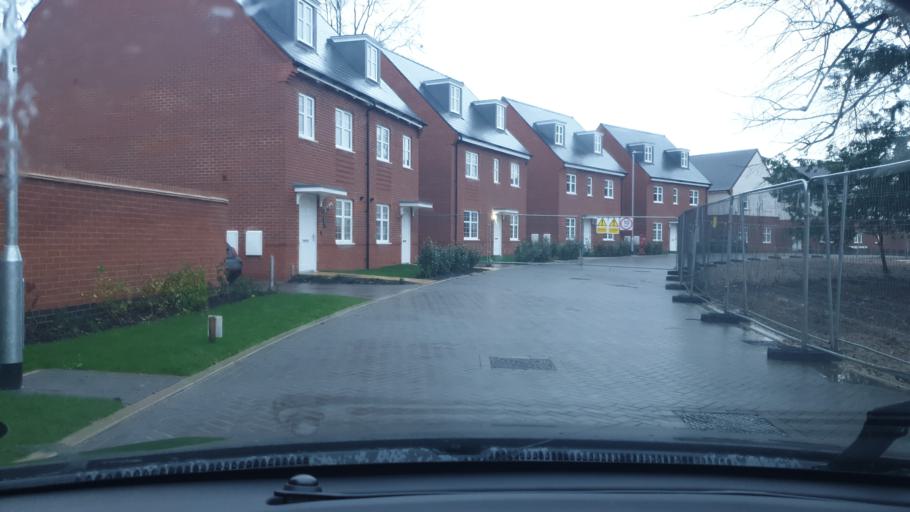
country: GB
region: England
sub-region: Essex
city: Great Horkesley
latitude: 51.9197
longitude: 0.8941
